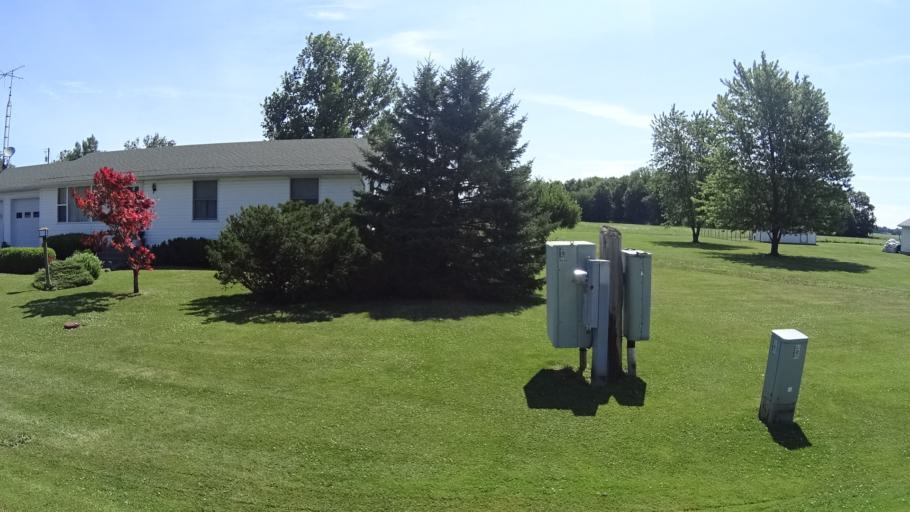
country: US
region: Ohio
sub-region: Ottawa County
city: Port Clinton
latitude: 41.4283
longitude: -82.9013
